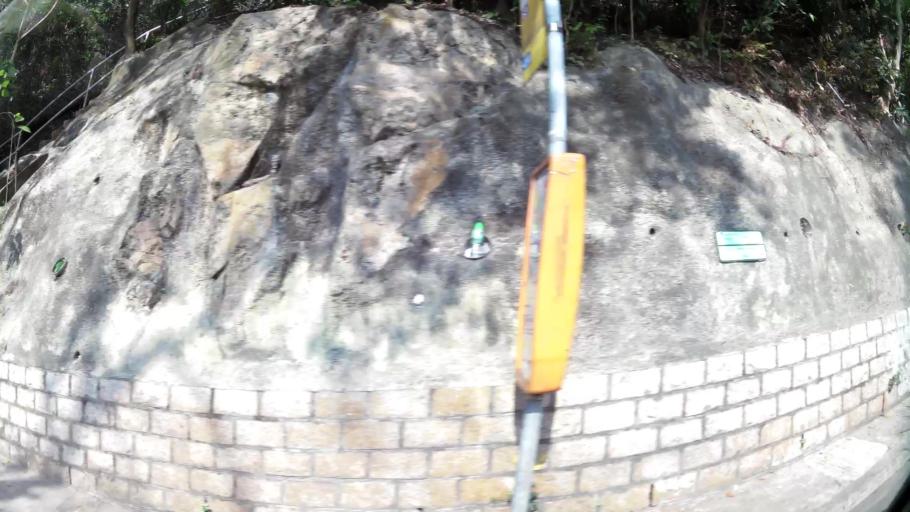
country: HK
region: Wanchai
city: Wan Chai
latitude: 22.2678
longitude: 114.1902
